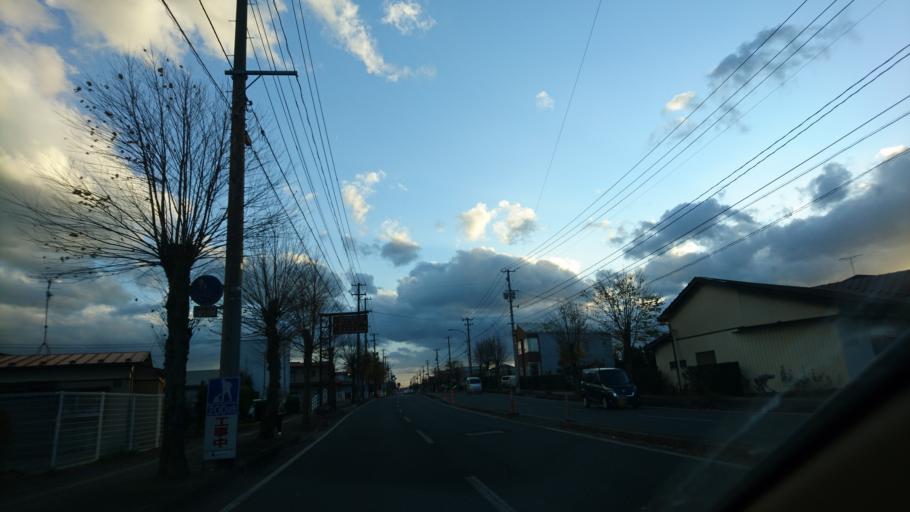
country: JP
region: Iwate
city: Mizusawa
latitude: 39.1481
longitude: 141.1315
